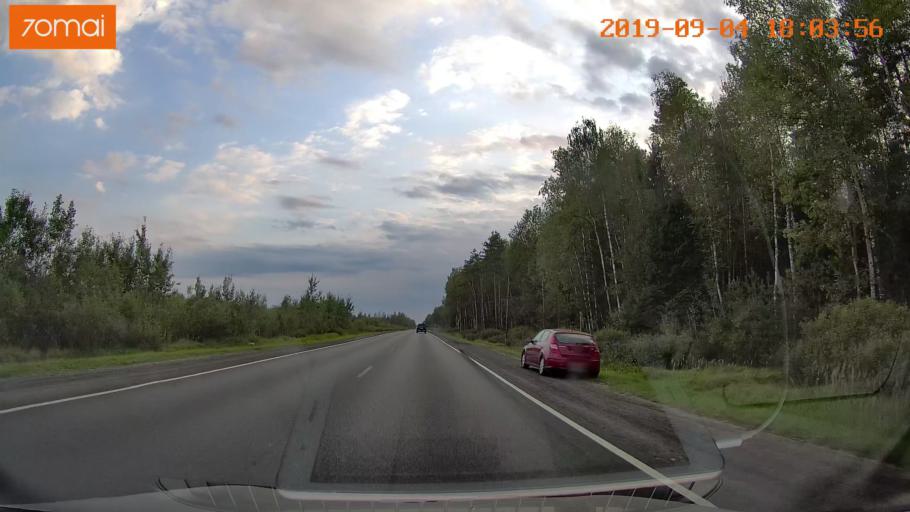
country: RU
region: Moskovskaya
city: Il'inskiy Pogost
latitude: 55.4580
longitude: 38.8458
